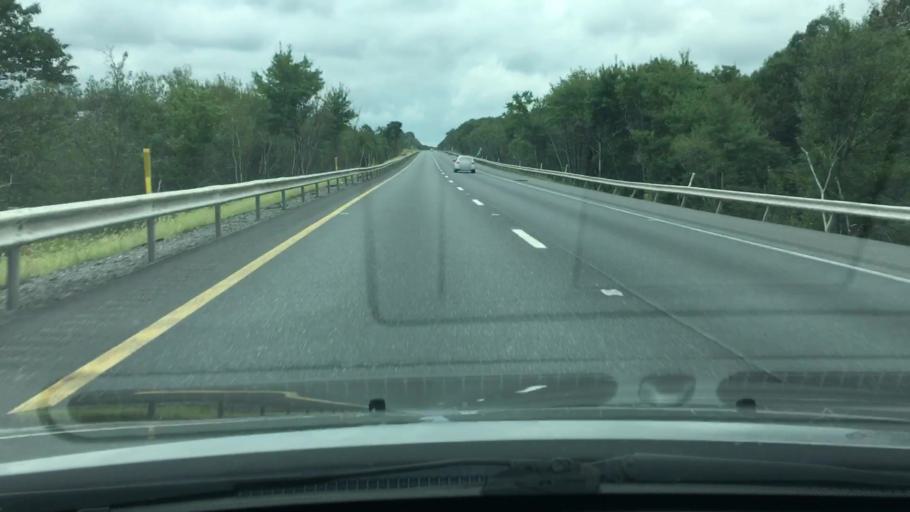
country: US
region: Pennsylvania
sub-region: Schuylkill County
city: Mahanoy City
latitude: 40.7925
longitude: -76.1319
